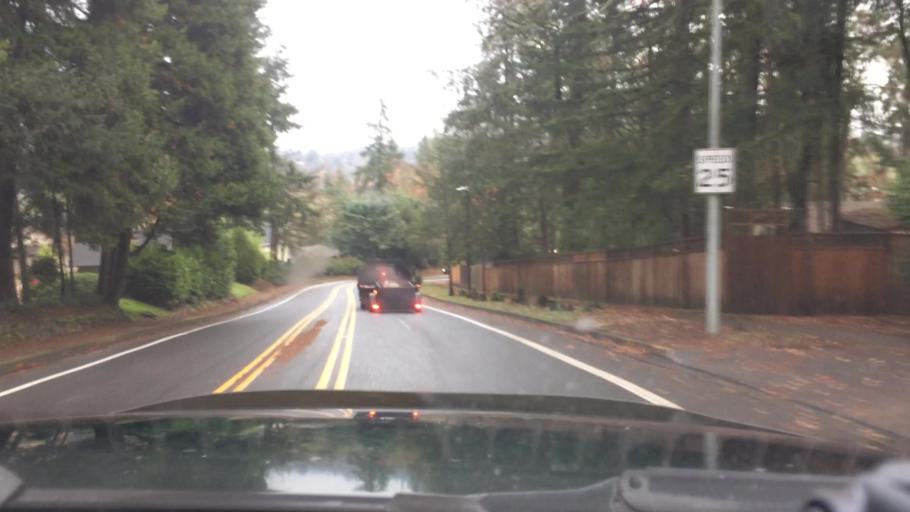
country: US
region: Oregon
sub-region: Lane County
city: Eugene
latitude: 44.0272
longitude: -123.1169
